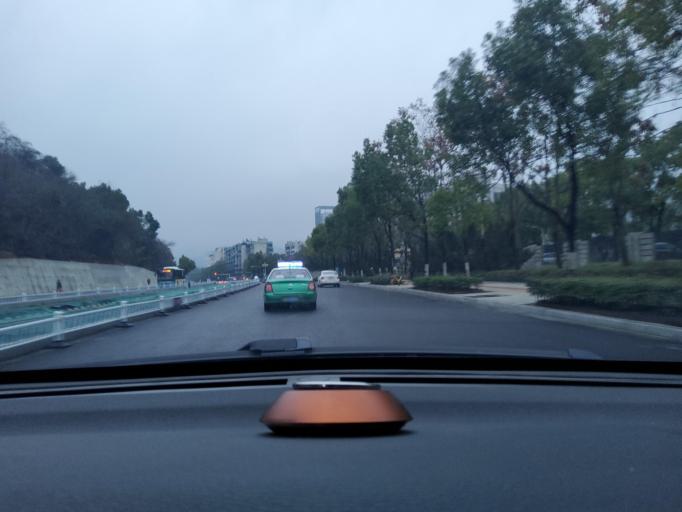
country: CN
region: Hubei
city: Tuanchengshan
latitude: 30.1934
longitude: 115.0246
